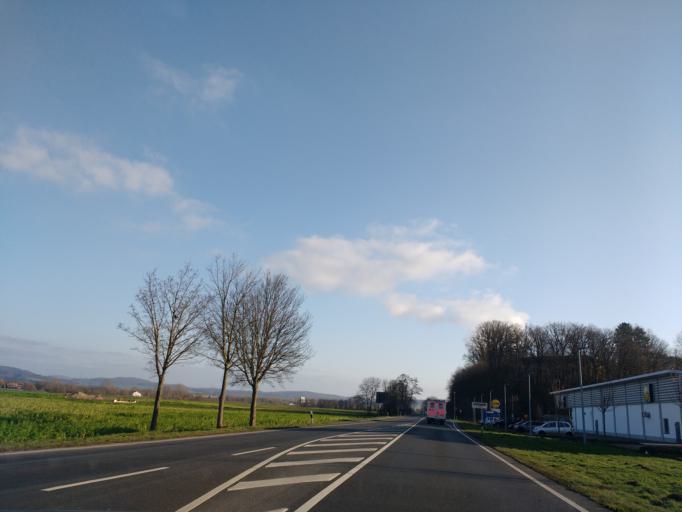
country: DE
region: Lower Saxony
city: Hameln
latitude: 52.0852
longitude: 9.3548
